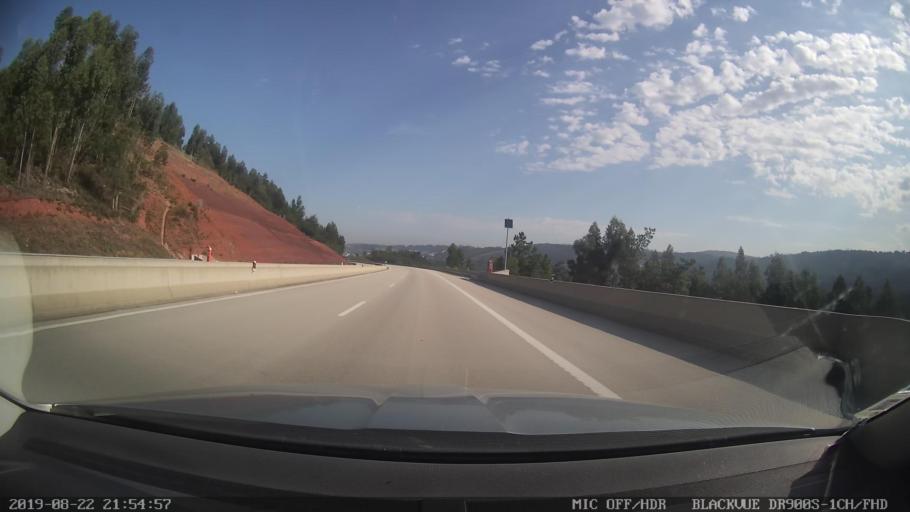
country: PT
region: Coimbra
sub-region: Coimbra
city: Coimbra
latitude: 40.1446
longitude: -8.3831
